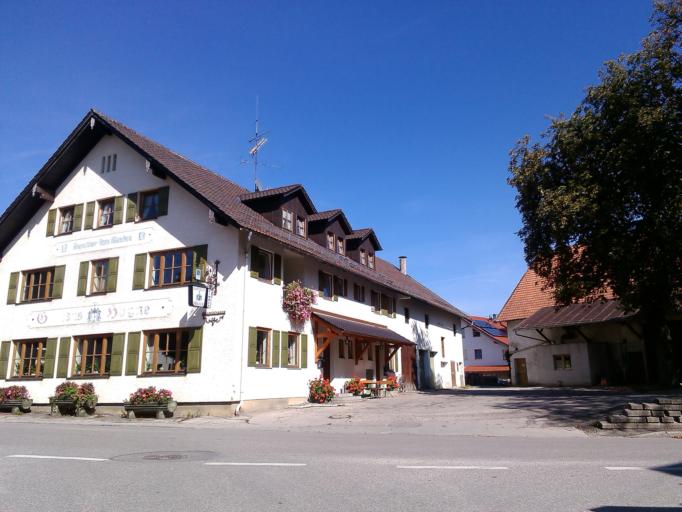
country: DE
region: Bavaria
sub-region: Upper Bavaria
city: Gilching
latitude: 48.0669
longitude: 11.3234
